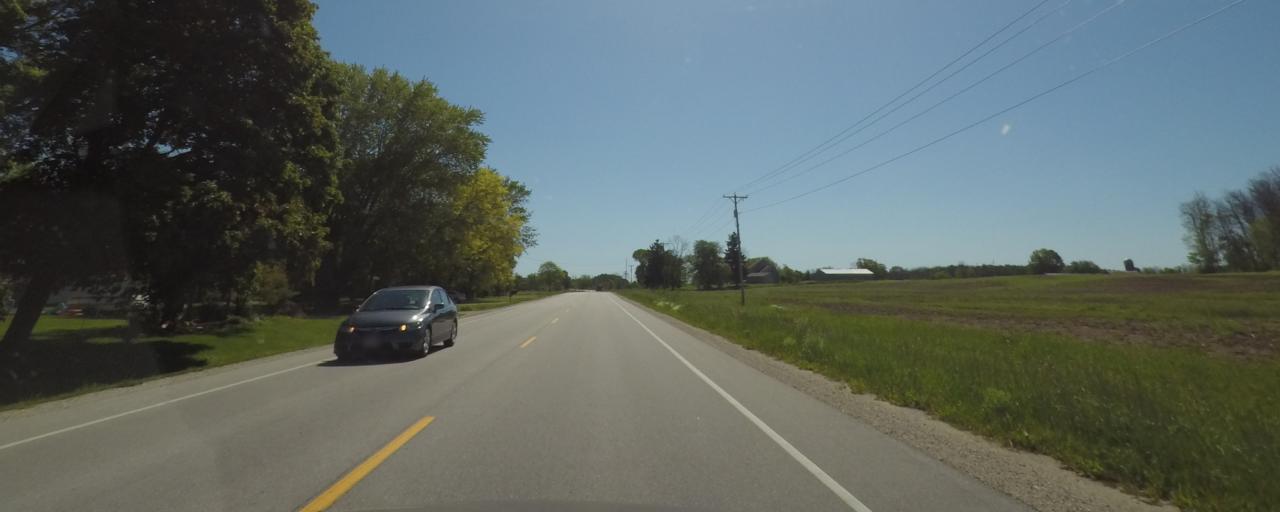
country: US
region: Wisconsin
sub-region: Sheboygan County
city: Plymouth
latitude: 43.7465
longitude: -87.9267
